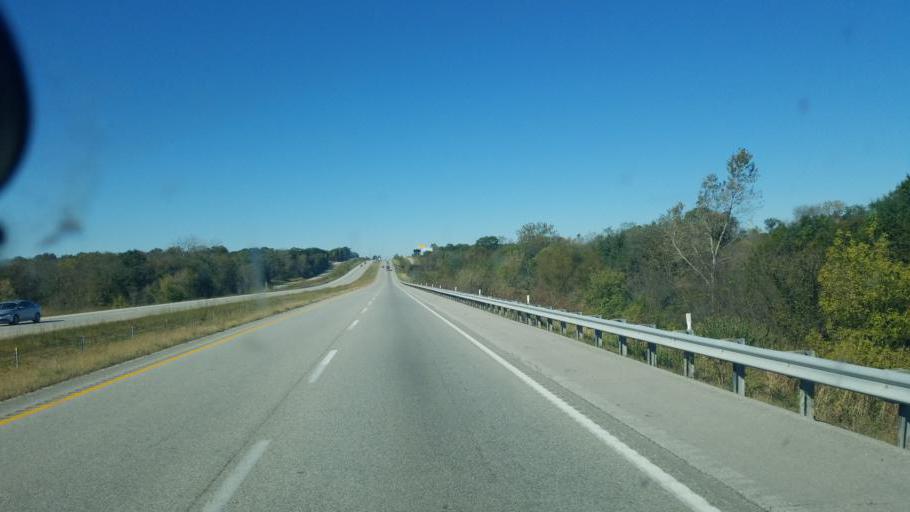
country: US
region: Missouri
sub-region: Saline County
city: Sweet Springs
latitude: 38.9746
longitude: -93.3595
